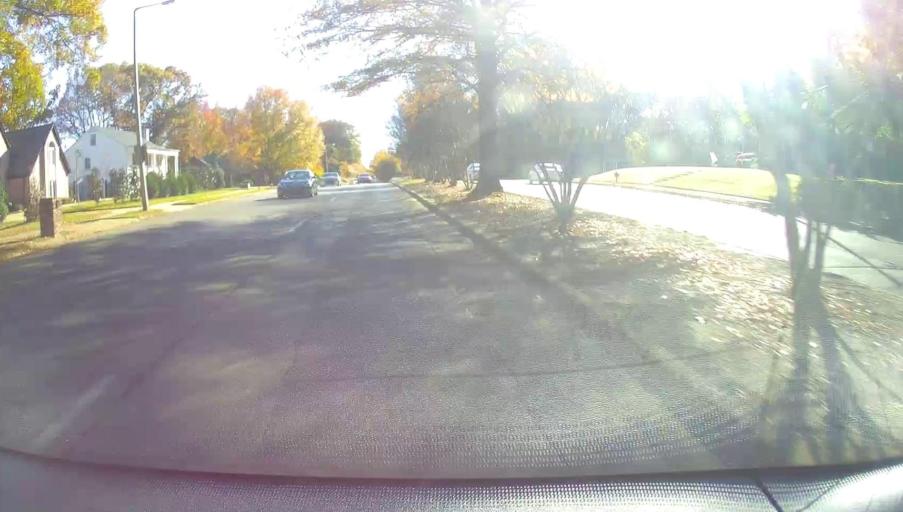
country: US
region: Tennessee
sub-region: Shelby County
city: Germantown
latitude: 35.0917
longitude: -89.8402
